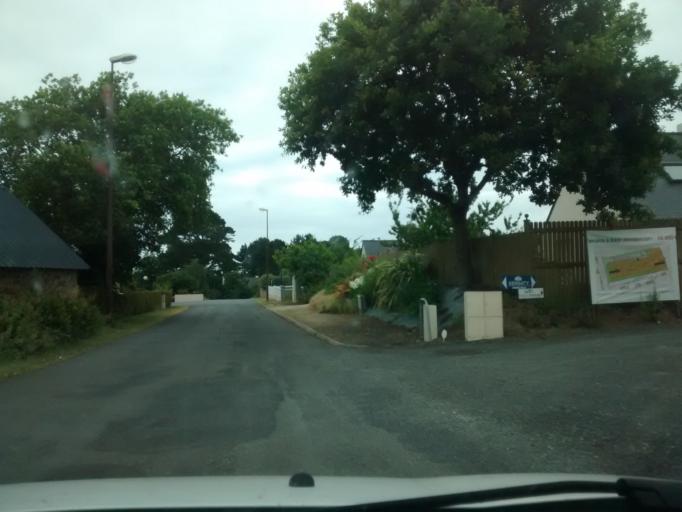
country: FR
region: Brittany
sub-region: Departement des Cotes-d'Armor
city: Louannec
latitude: 48.7965
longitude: -3.4135
